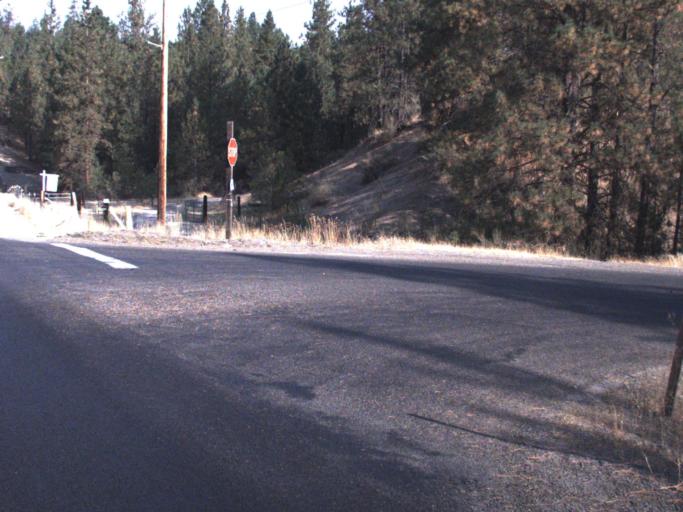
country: US
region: Washington
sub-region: Spokane County
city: Deer Park
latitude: 47.8385
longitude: -117.6075
